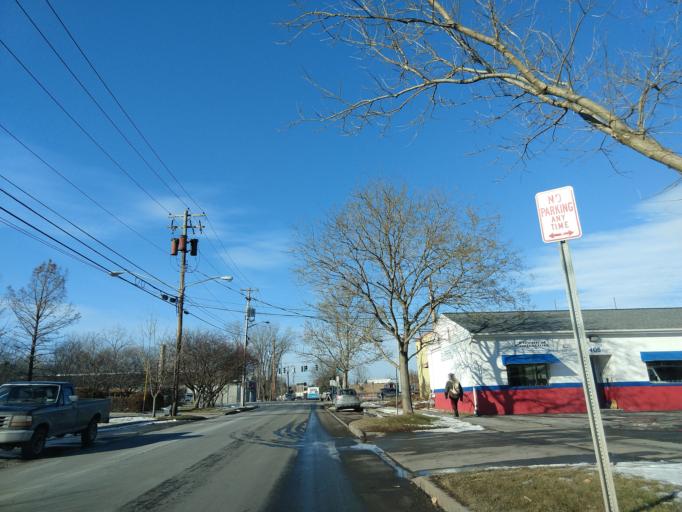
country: US
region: New York
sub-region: Tompkins County
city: Ithaca
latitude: 42.4477
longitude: -76.5061
